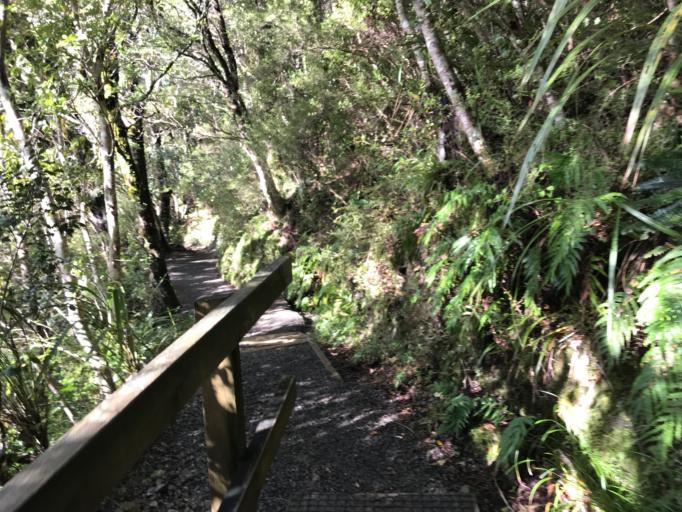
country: NZ
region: Wellington
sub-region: Masterton District
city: Masterton
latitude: -40.9032
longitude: 175.4544
